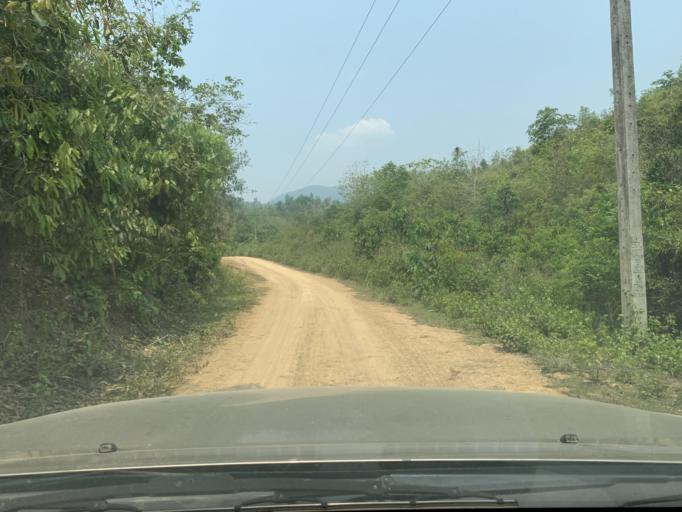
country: LA
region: Louangphabang
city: Louangphabang
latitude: 19.9517
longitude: 102.1291
